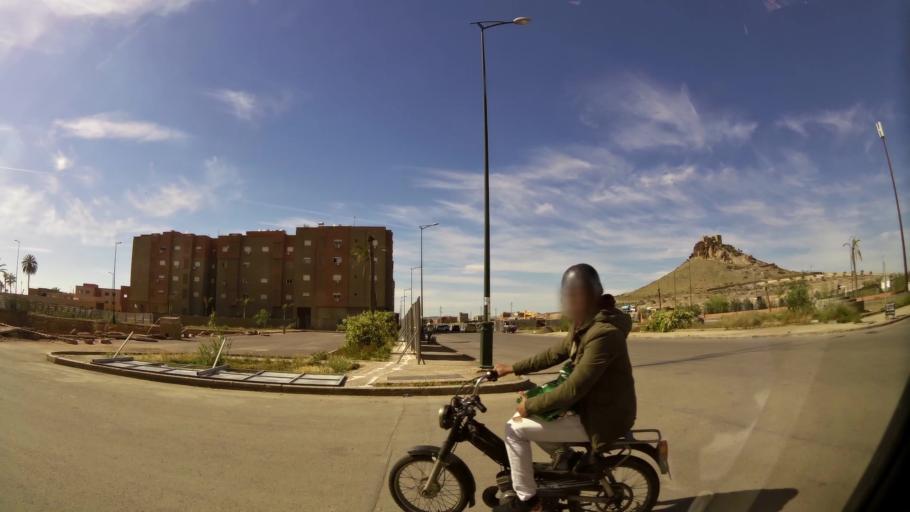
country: MA
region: Marrakech-Tensift-Al Haouz
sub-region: Marrakech
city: Marrakesh
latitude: 31.6600
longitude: -8.0227
